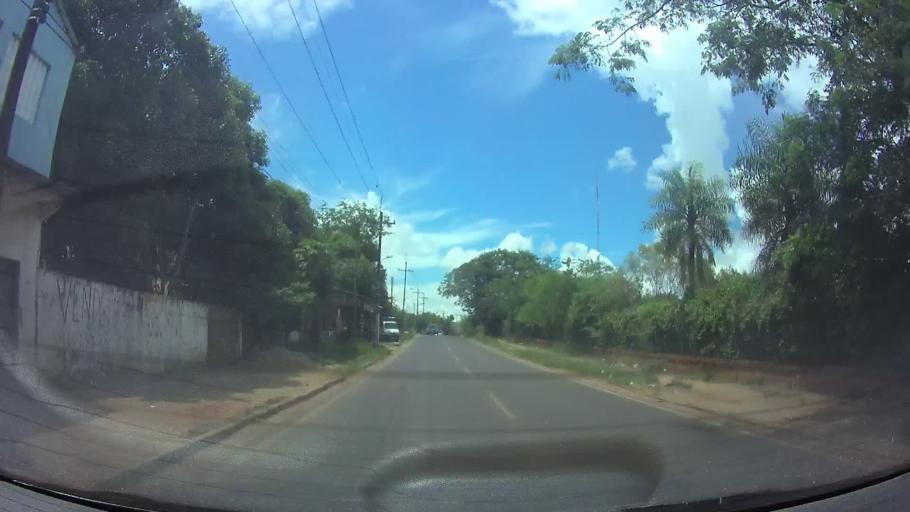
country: PY
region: Central
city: San Lorenzo
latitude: -25.2976
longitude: -57.4917
